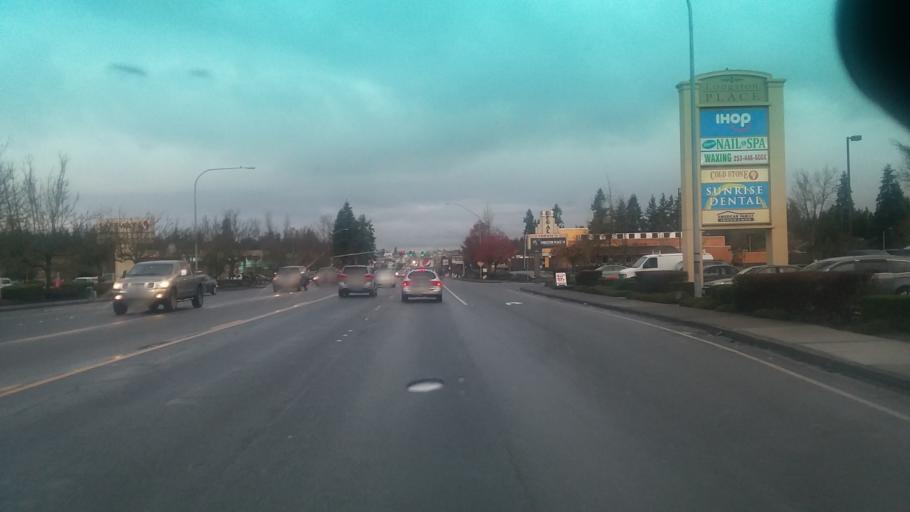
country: US
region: Washington
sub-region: Pierce County
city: South Hill
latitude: 47.1348
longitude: -122.2929
